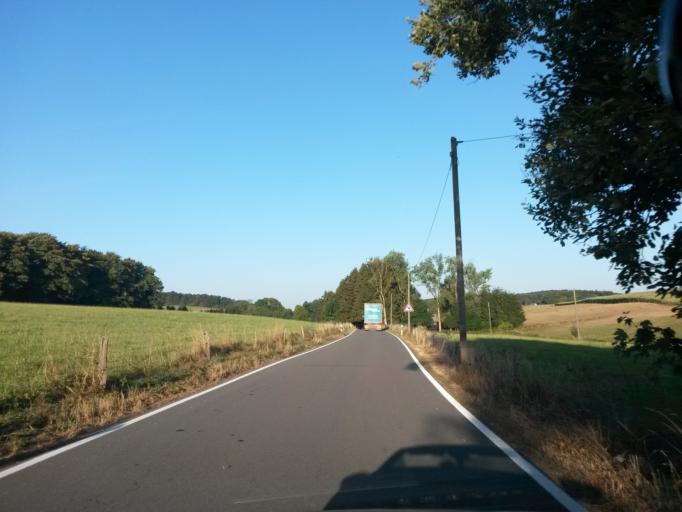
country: DE
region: North Rhine-Westphalia
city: Wipperfurth
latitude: 51.1003
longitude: 7.4560
